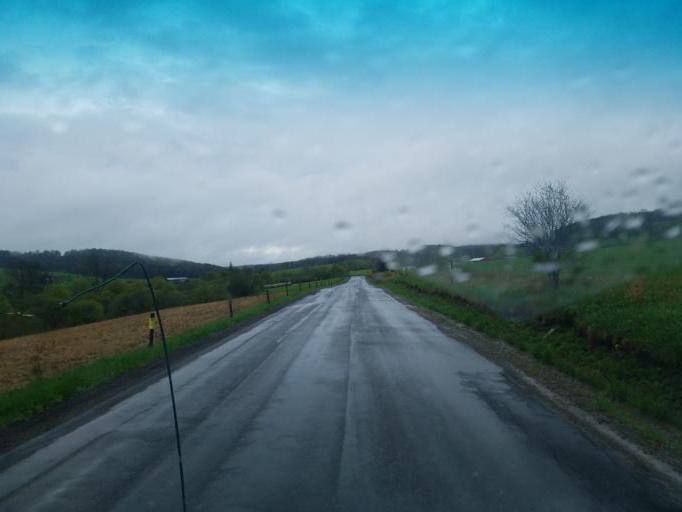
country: US
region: Pennsylvania
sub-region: Tioga County
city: Westfield
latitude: 41.9679
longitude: -77.6567
